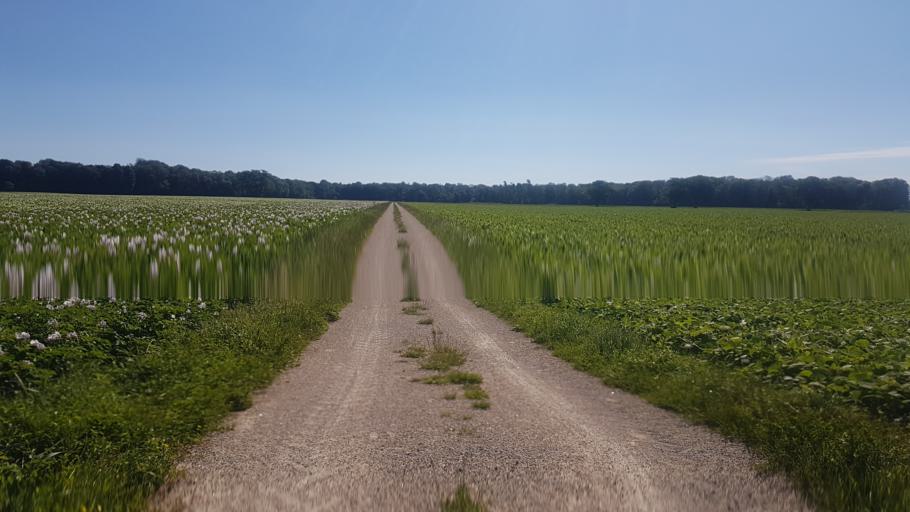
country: DE
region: Bavaria
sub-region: Upper Bavaria
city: Weichering
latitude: 48.7296
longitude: 11.2895
